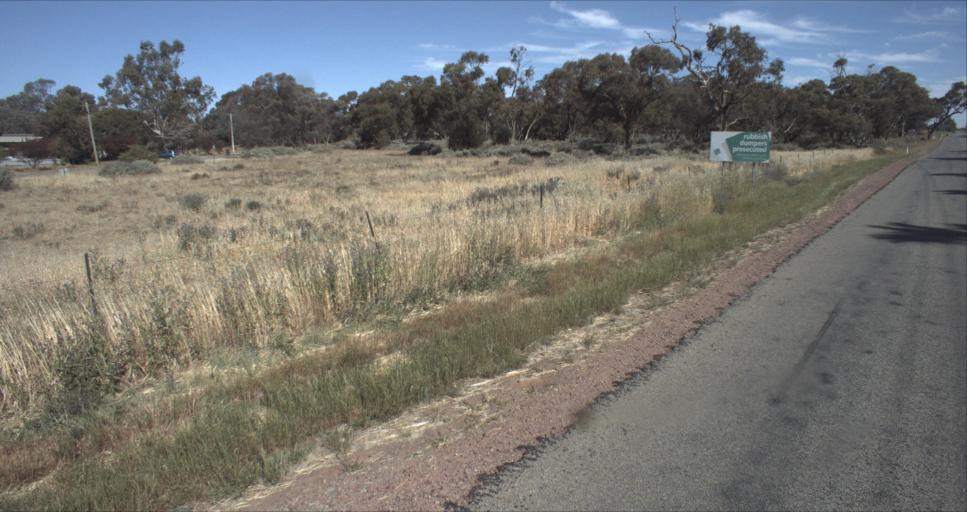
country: AU
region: New South Wales
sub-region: Leeton
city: Leeton
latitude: -34.5566
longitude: 146.3844
